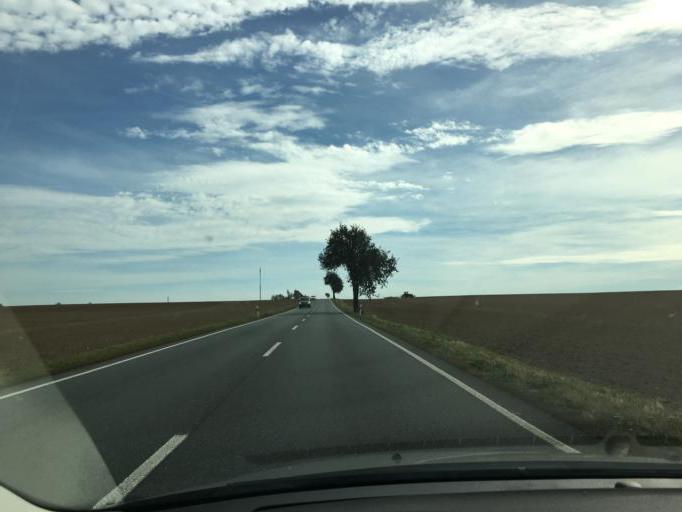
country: DE
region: Saxony
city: Lommatzsch
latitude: 51.2187
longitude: 13.3670
